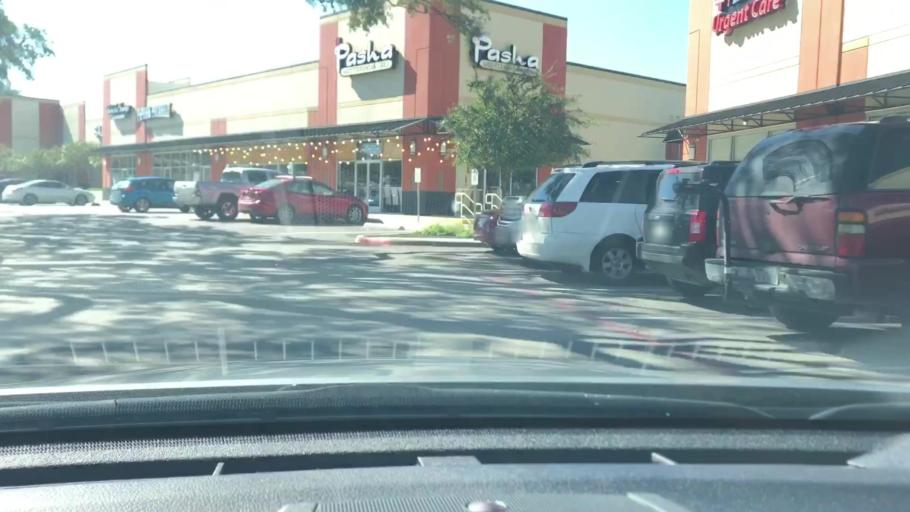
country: US
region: Texas
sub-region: Bexar County
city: Live Oak
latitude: 29.5759
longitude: -98.3249
